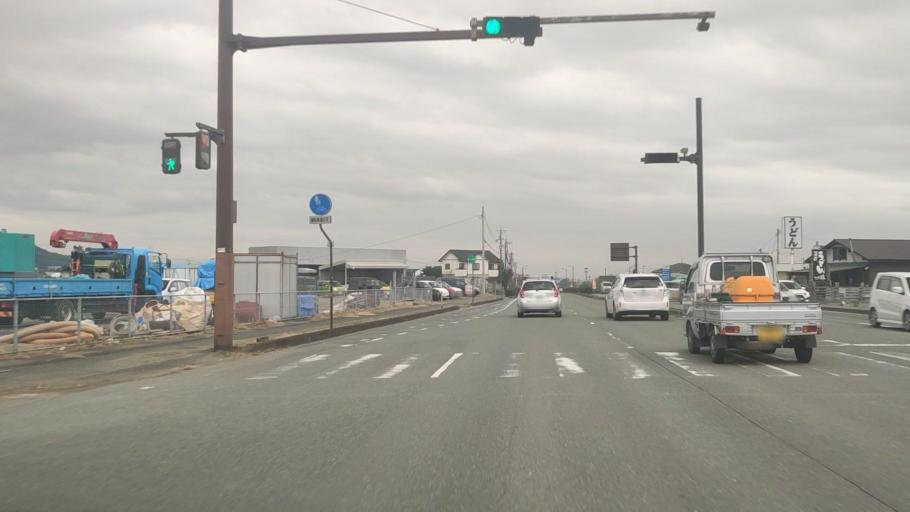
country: JP
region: Kumamoto
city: Ozu
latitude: 32.8335
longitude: 130.8004
